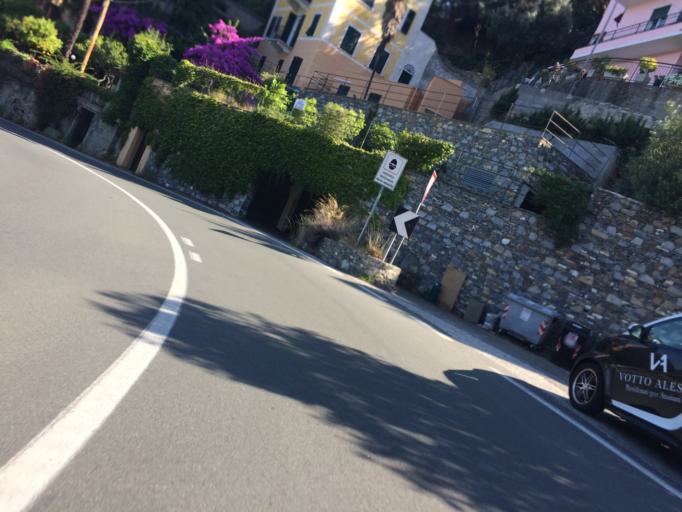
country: IT
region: Liguria
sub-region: Provincia di Genova
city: Camogli
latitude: 44.3556
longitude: 9.1555
